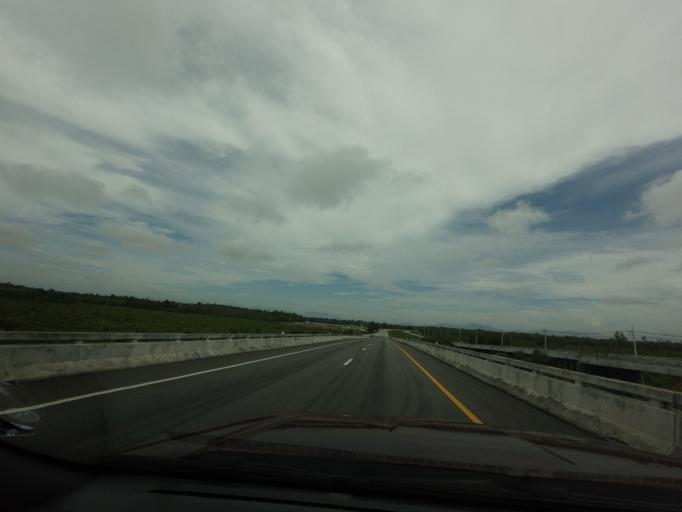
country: TH
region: Narathiwat
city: Narathiwat
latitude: 6.3462
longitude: 101.8400
